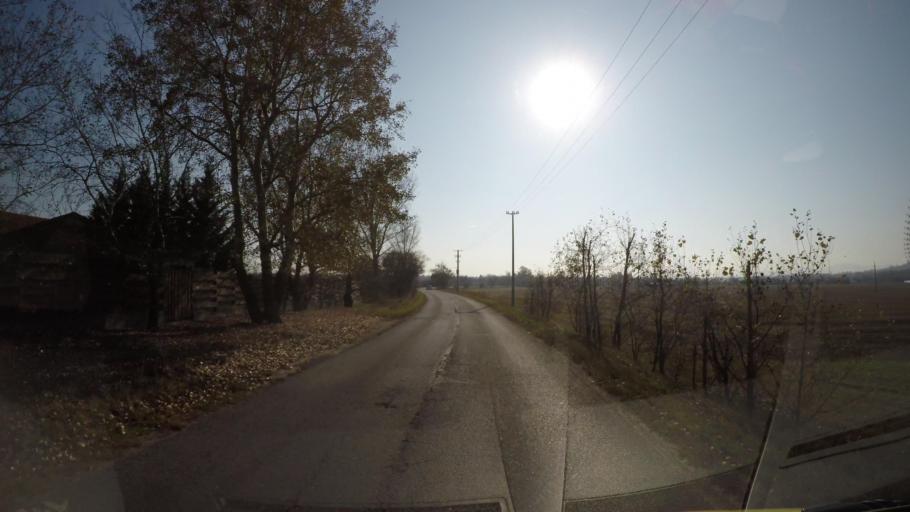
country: HU
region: Pest
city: Leanyfalu
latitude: 47.6971
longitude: 19.1039
